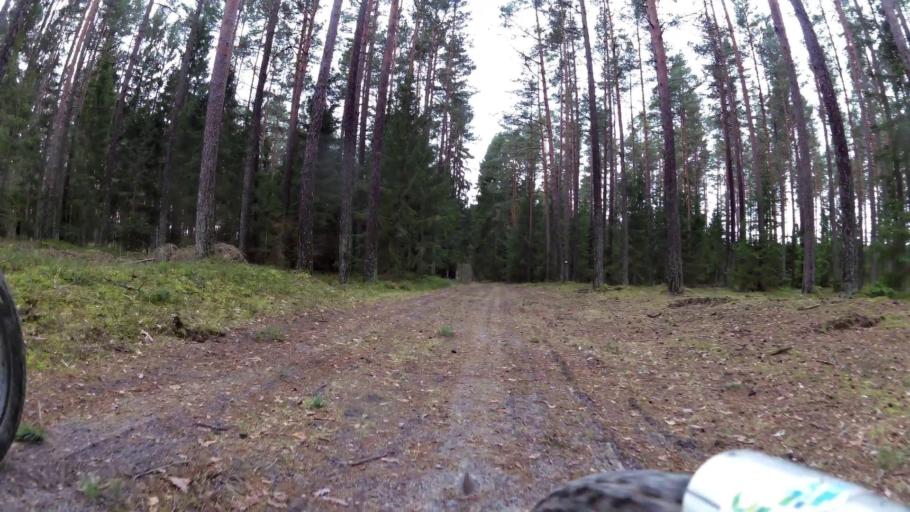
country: PL
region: Pomeranian Voivodeship
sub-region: Powiat bytowski
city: Kolczyglowy
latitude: 54.1574
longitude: 17.1884
